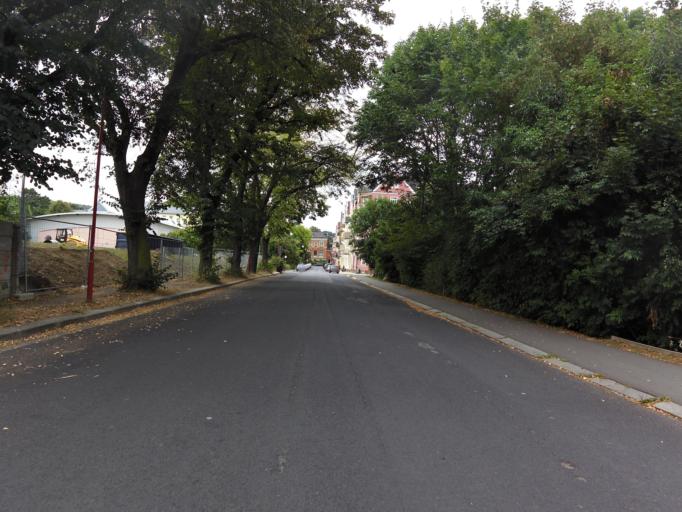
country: DE
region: Saxony
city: Dobeln
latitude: 51.1190
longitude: 13.1273
